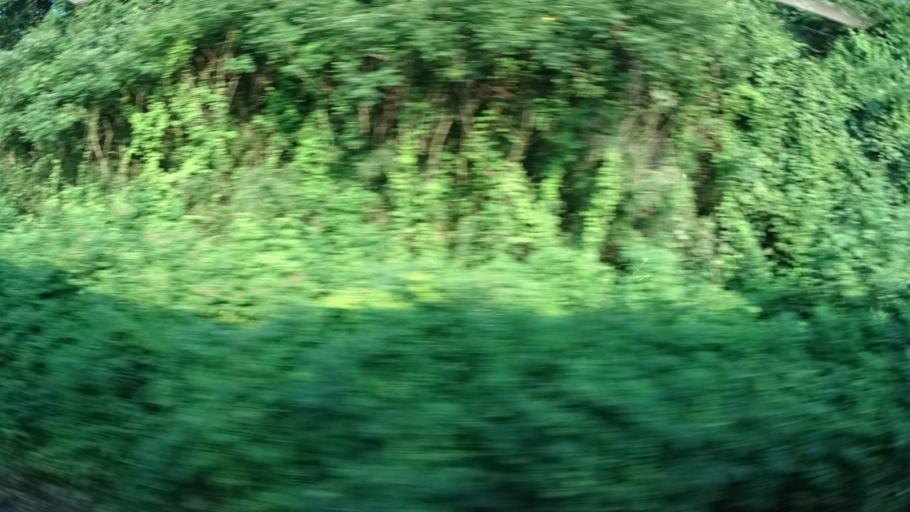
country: JP
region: Ibaraki
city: Funaishikawa
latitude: 36.4449
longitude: 140.5468
